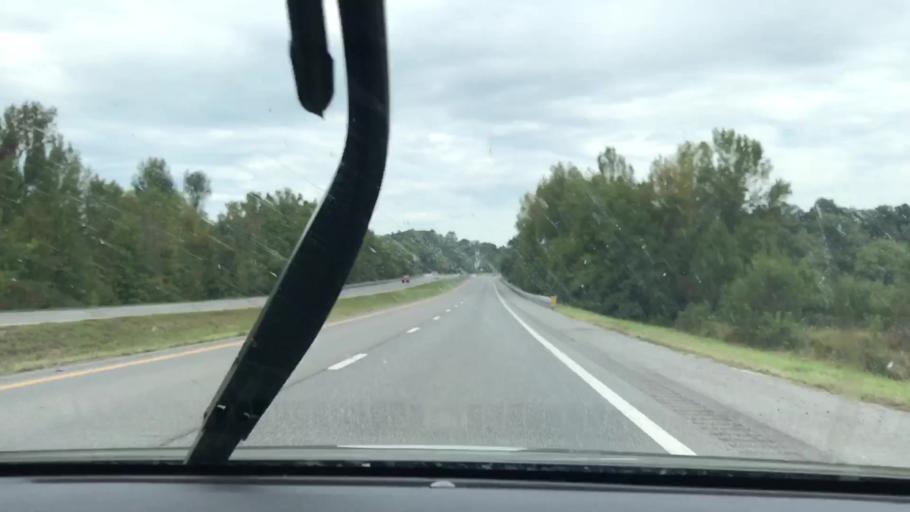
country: US
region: Kentucky
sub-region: Marshall County
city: Benton
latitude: 36.8124
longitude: -88.4888
